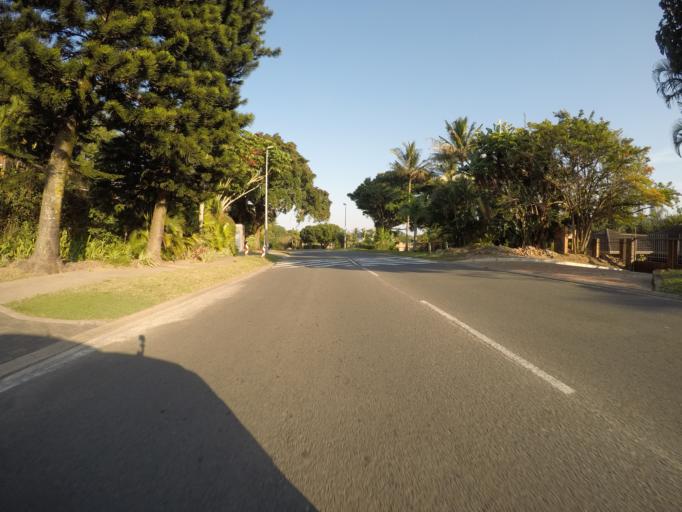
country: ZA
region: KwaZulu-Natal
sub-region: uThungulu District Municipality
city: Richards Bay
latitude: -28.7727
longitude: 32.1125
